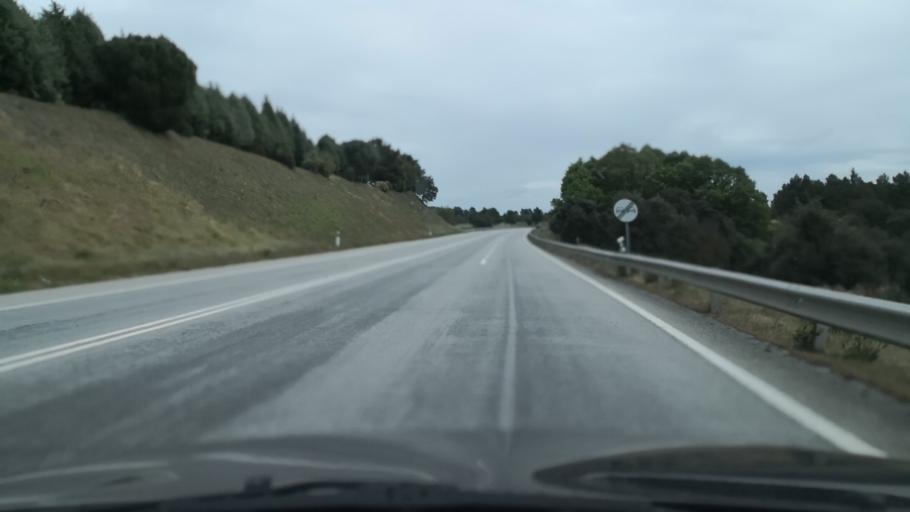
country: PT
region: Guarda
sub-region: Celorico da Beira
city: Celorico da Beira
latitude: 40.6353
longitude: -7.3189
